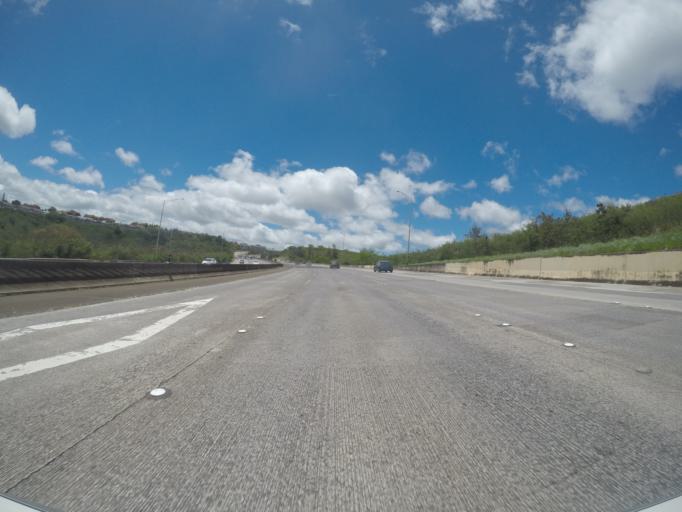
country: US
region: Hawaii
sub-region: Honolulu County
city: Waipio
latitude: 21.4118
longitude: -157.9897
